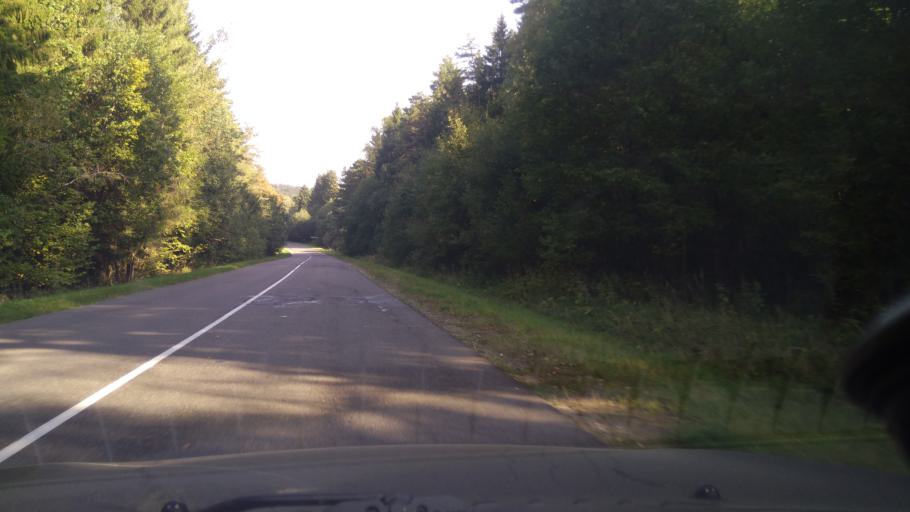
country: BY
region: Minsk
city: Rakaw
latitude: 54.0215
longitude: 27.0526
